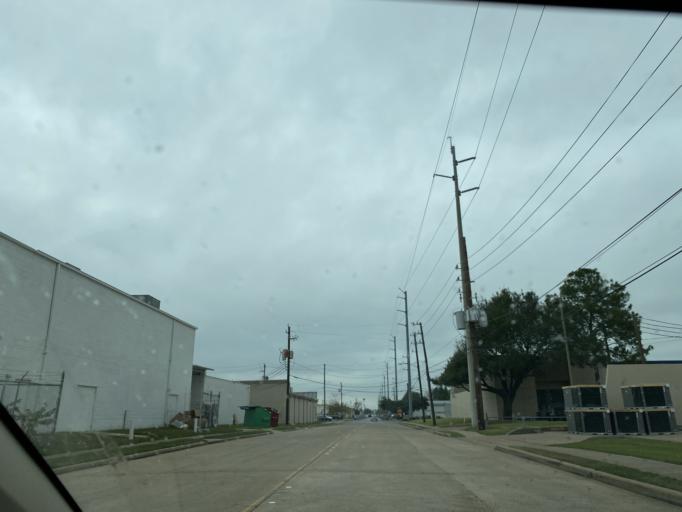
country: US
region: Texas
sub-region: Harris County
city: Piney Point Village
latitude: 29.7227
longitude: -95.5194
